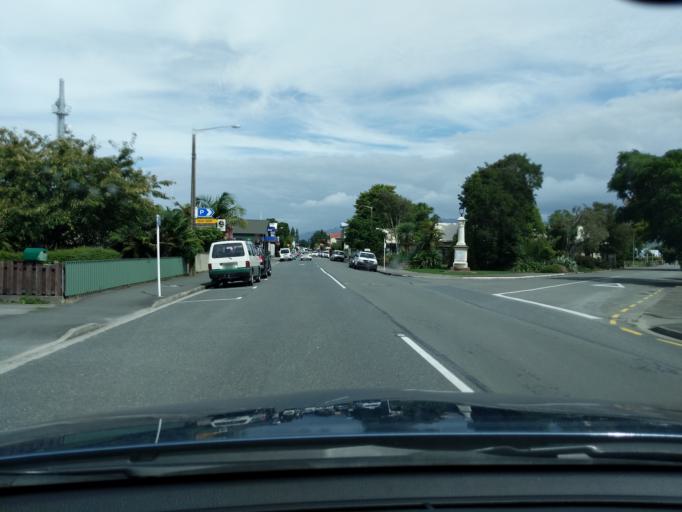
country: NZ
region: Tasman
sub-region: Tasman District
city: Takaka
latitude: -40.8570
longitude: 172.8065
